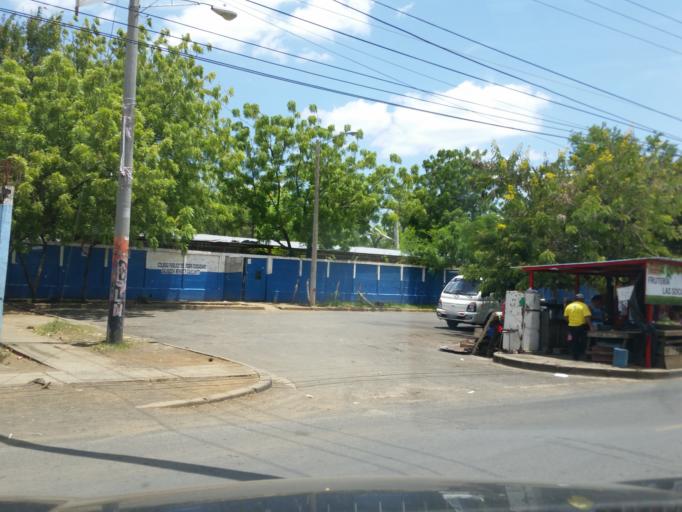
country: NI
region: Managua
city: Managua
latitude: 12.1153
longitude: -86.2495
